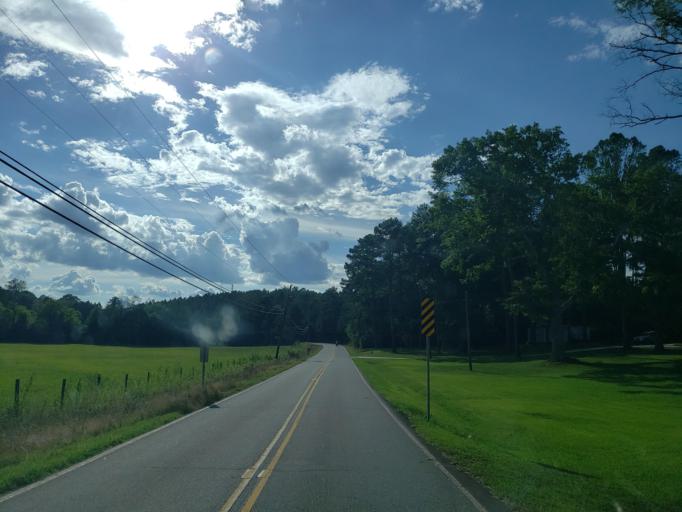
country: US
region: Georgia
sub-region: Floyd County
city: Lindale
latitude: 34.2021
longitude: -85.0922
